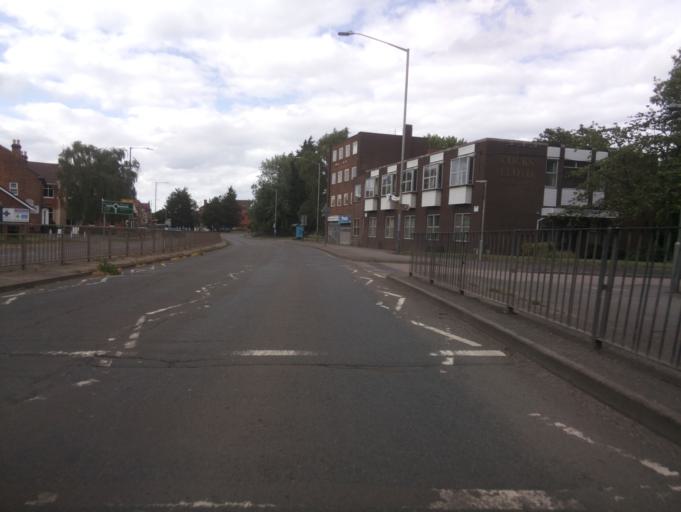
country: GB
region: England
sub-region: Warwickshire
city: Nuneaton
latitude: 52.5192
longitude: -1.4670
